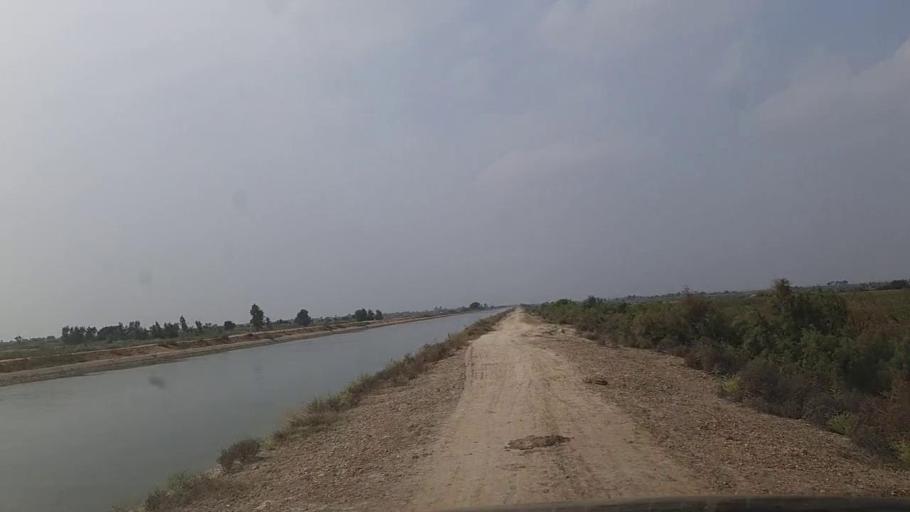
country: PK
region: Sindh
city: Thatta
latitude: 24.8052
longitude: 67.8911
